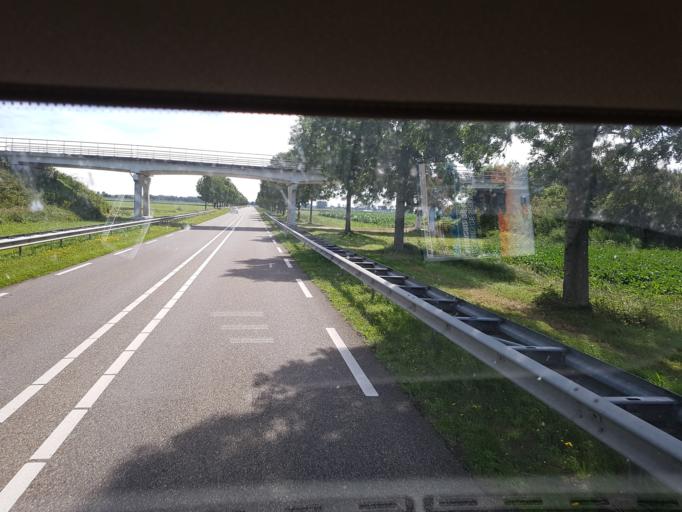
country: NL
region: North Brabant
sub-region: Gemeente Aalburg
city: Aalburg
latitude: 51.7705
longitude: 5.0720
